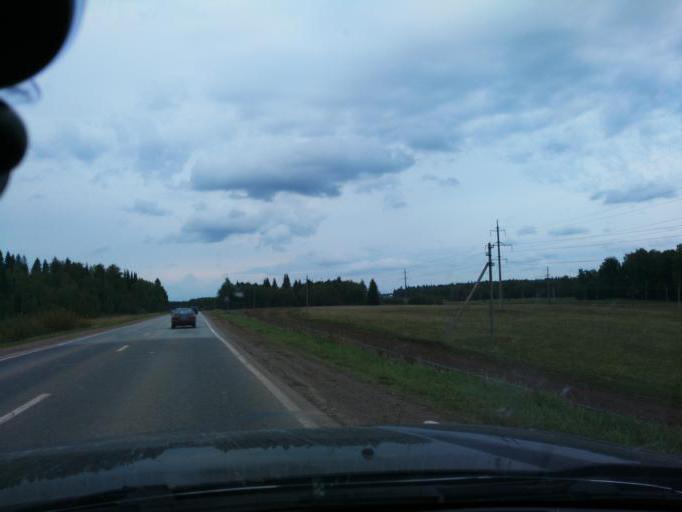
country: RU
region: Perm
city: Chernushka
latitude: 56.5309
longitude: 56.0478
